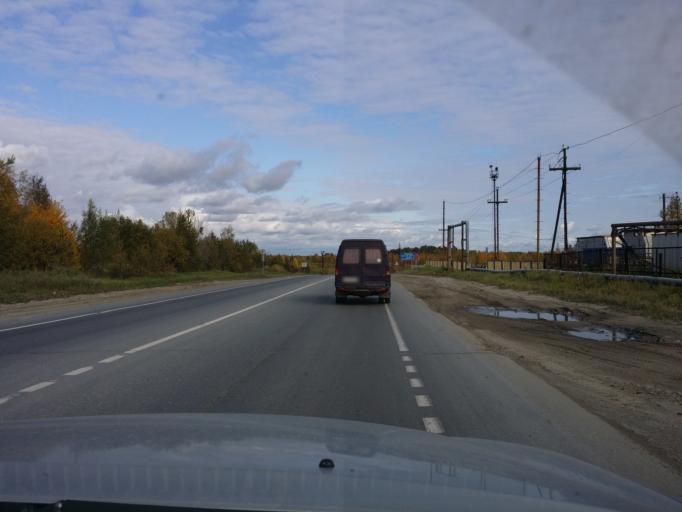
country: RU
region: Khanty-Mansiyskiy Avtonomnyy Okrug
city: Megion
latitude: 61.0547
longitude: 76.1132
